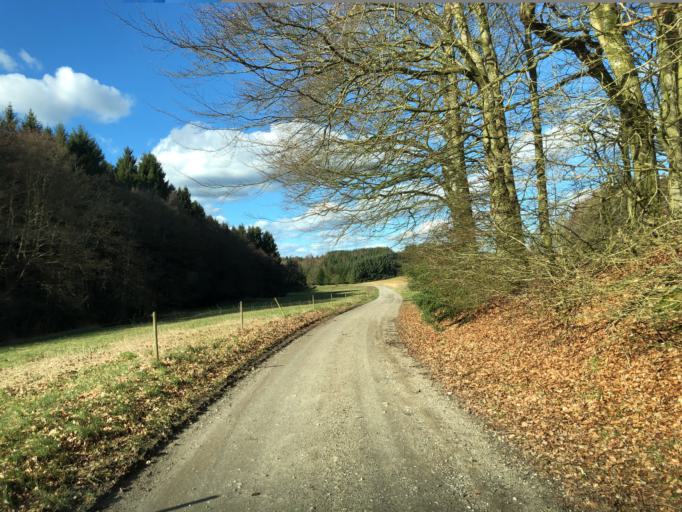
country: DK
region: Central Jutland
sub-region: Favrskov Kommune
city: Hammel
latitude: 56.3076
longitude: 9.9163
